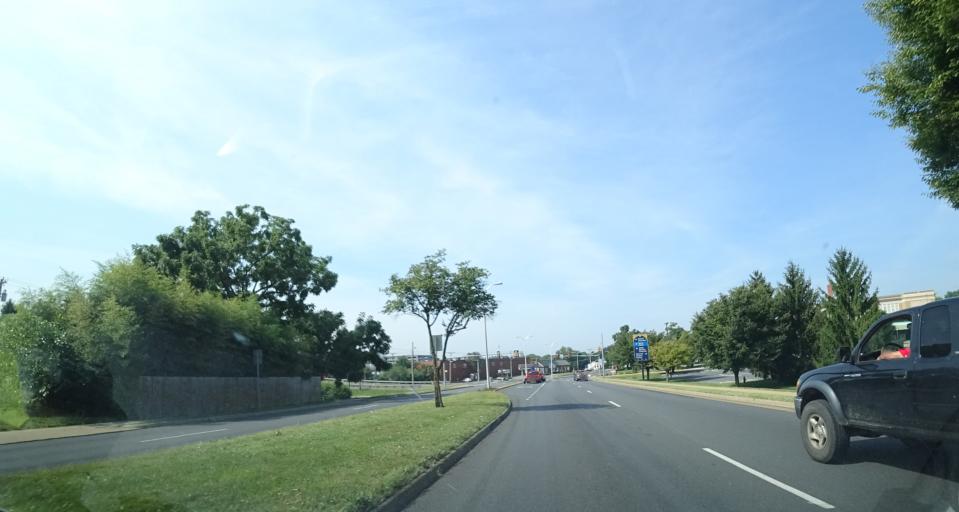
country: US
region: Virginia
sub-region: City of Harrisonburg
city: Harrisonburg
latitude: 38.4455
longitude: -78.8764
